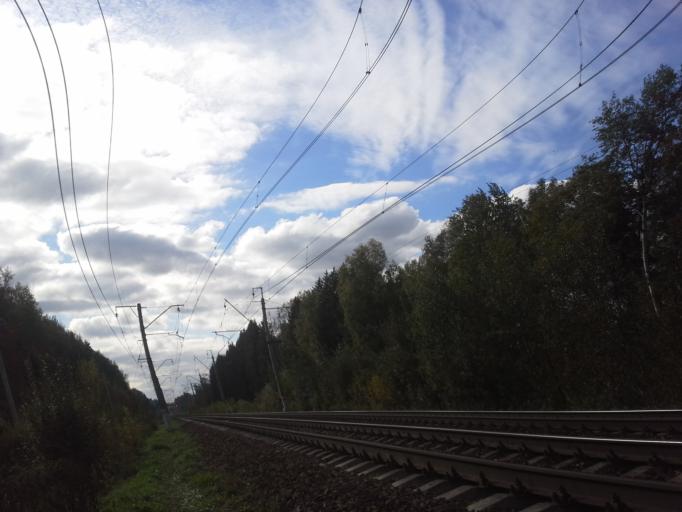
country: RU
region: Moskovskaya
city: Krasnoznamensk
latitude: 55.6313
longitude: 37.0485
